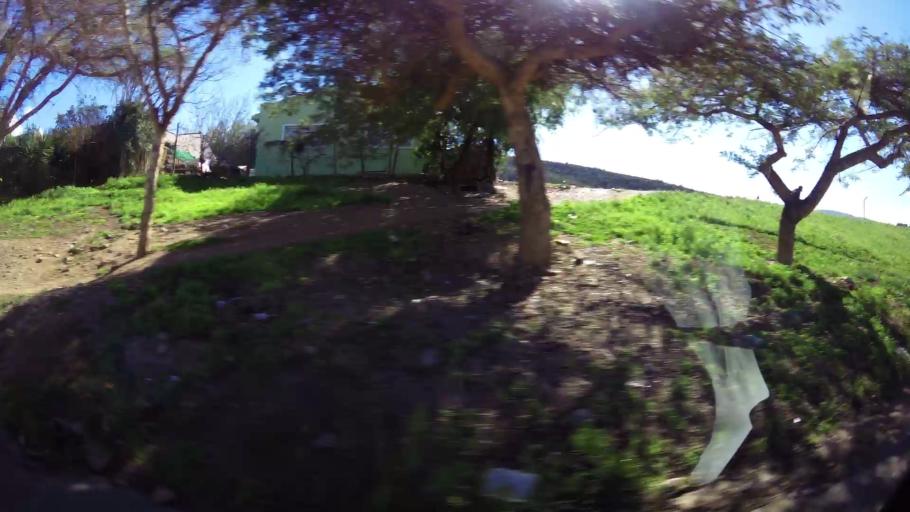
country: ZA
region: Western Cape
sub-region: Cape Winelands District Municipality
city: Ashton
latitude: -33.7819
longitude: 20.1266
